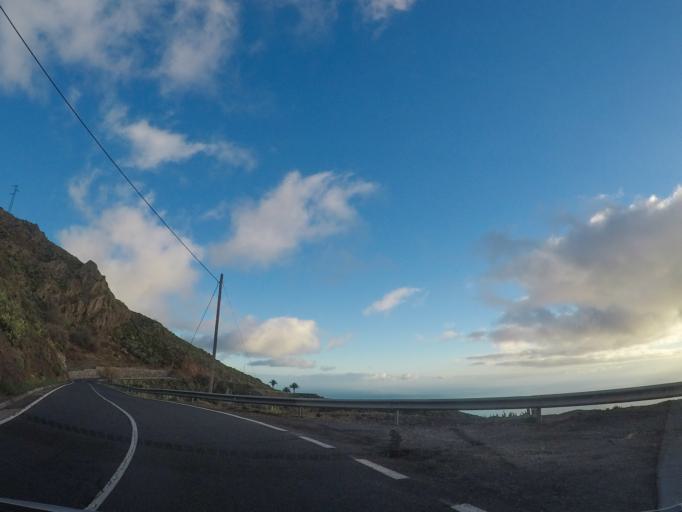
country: ES
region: Canary Islands
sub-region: Provincia de Santa Cruz de Tenerife
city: Alajero
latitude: 28.0799
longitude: -17.2439
